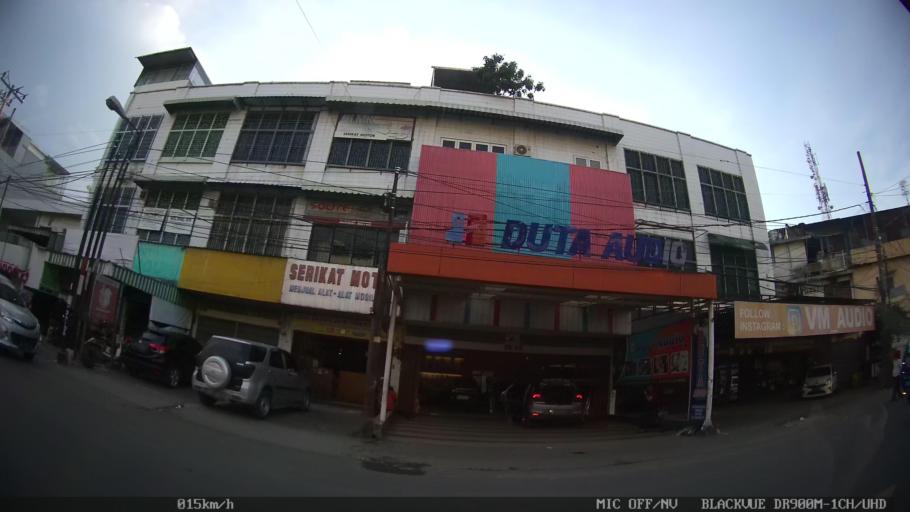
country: ID
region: North Sumatra
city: Medan
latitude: 3.5911
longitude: 98.6688
